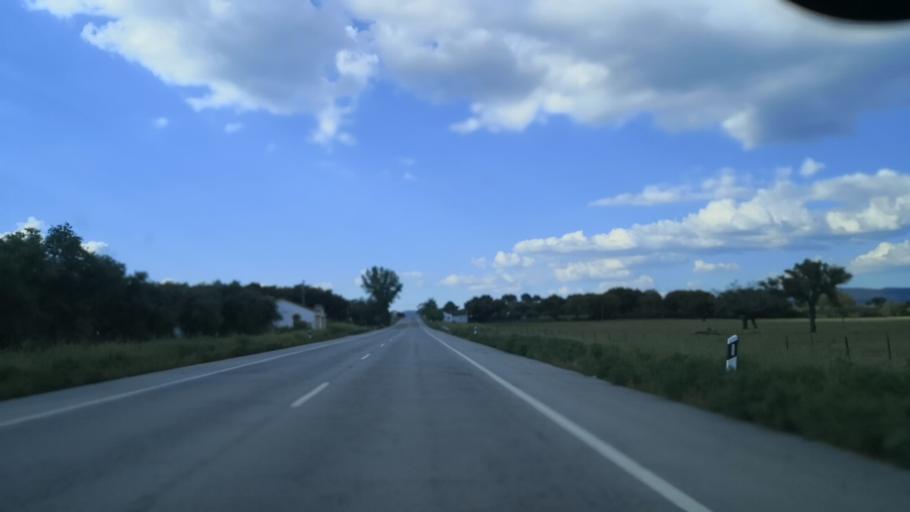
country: PT
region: Portalegre
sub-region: Portalegre
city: Urra
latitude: 39.2328
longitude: -7.4537
